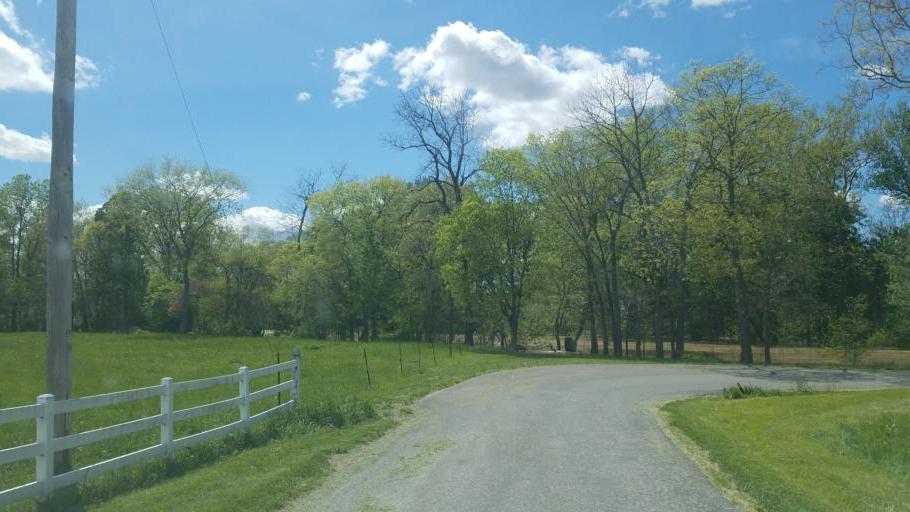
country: US
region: Ohio
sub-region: Marion County
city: Prospect
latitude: 40.3855
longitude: -83.1877
